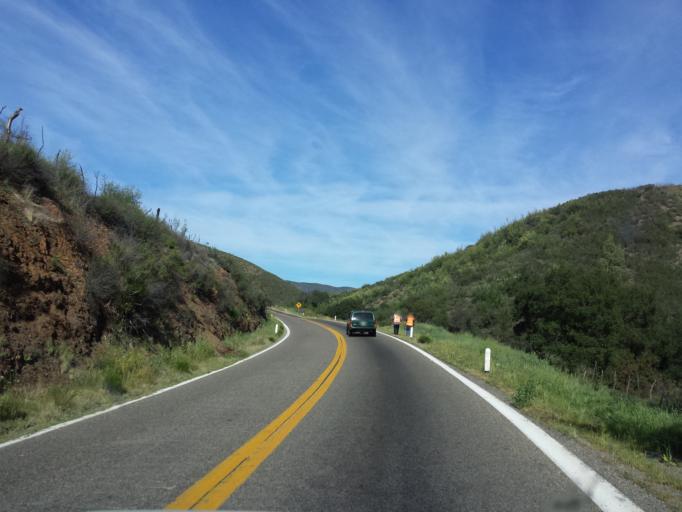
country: MX
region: Baja California
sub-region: Ensenada
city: Rancho Verde
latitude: 32.1845
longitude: -116.4925
